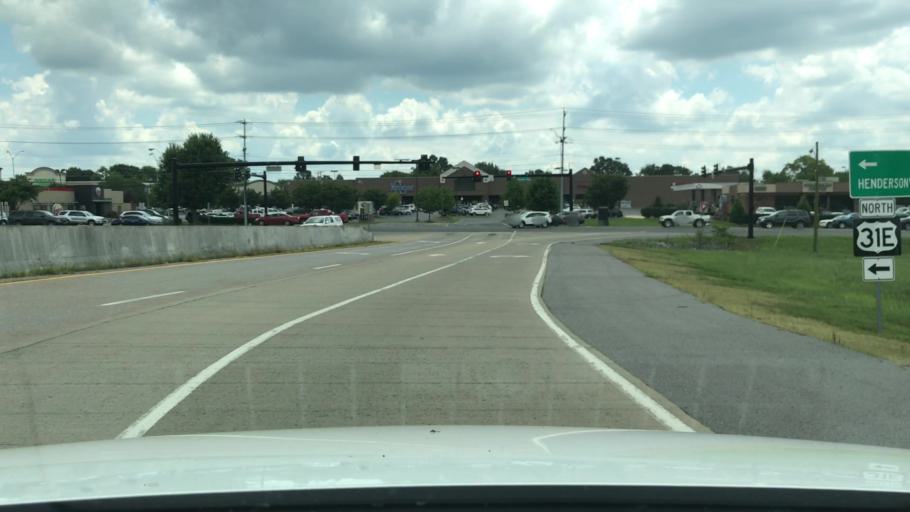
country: US
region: Tennessee
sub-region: Sumner County
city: Gallatin
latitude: 36.3800
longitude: -86.4671
